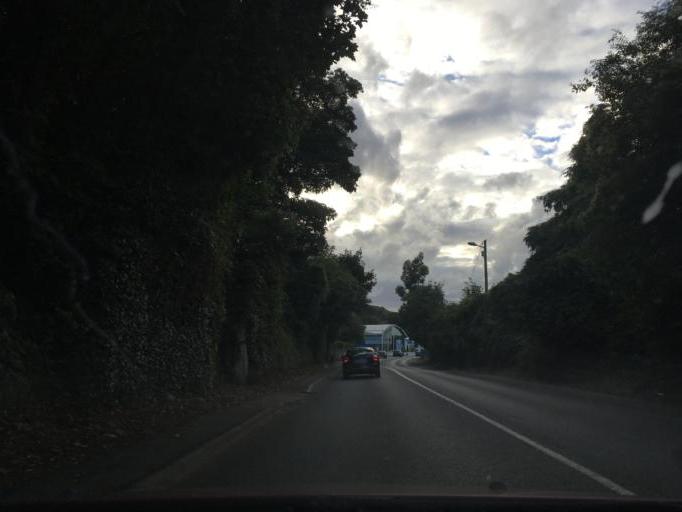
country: IE
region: Leinster
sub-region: Wicklow
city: Wicklow
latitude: 52.9861
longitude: -6.0570
